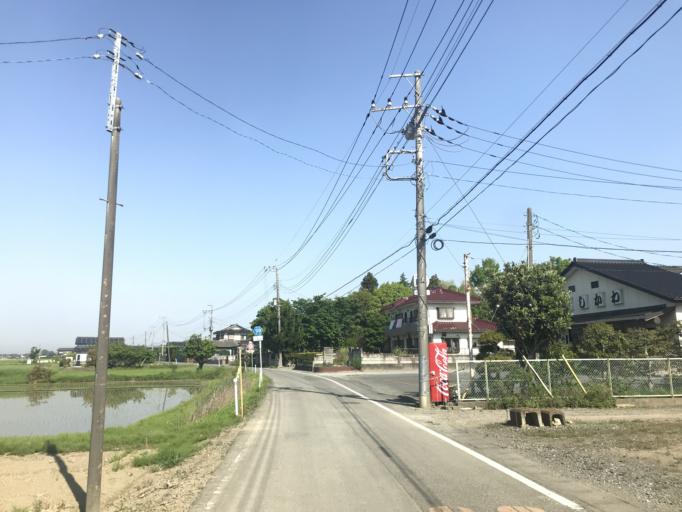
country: JP
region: Ibaraki
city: Mitsukaido
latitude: 36.0577
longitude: 140.0143
